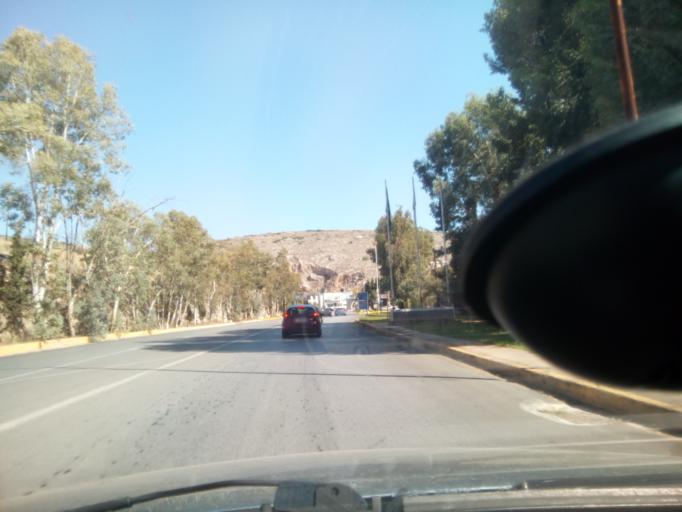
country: GR
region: Central Greece
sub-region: Nomos Evvoias
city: Chalkida
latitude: 38.4485
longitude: 23.6203
